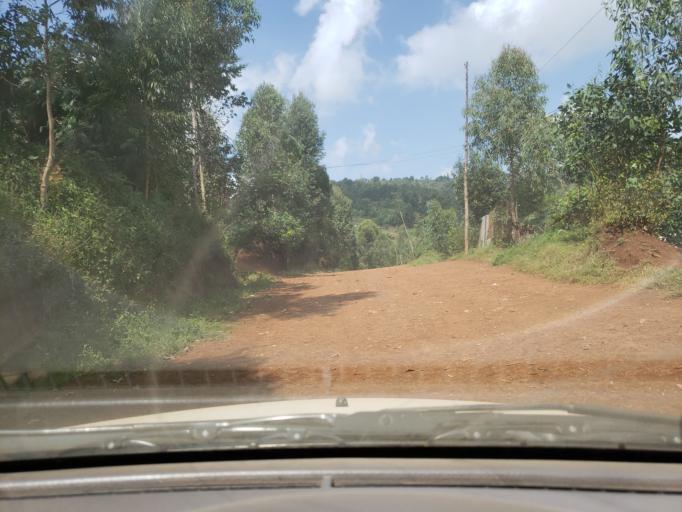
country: CD
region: South Kivu
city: Bukavu
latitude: -2.5066
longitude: 28.8272
